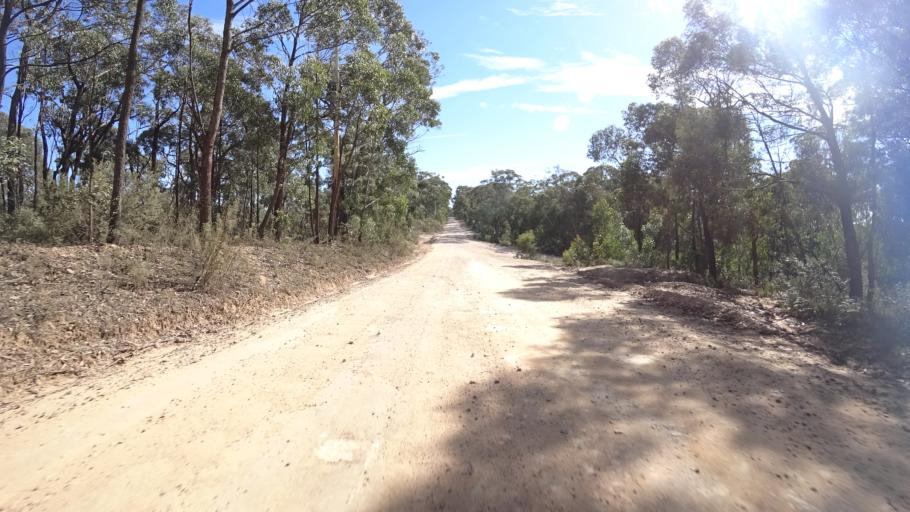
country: AU
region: New South Wales
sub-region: Lithgow
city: Lithgow
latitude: -33.4228
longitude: 150.2022
